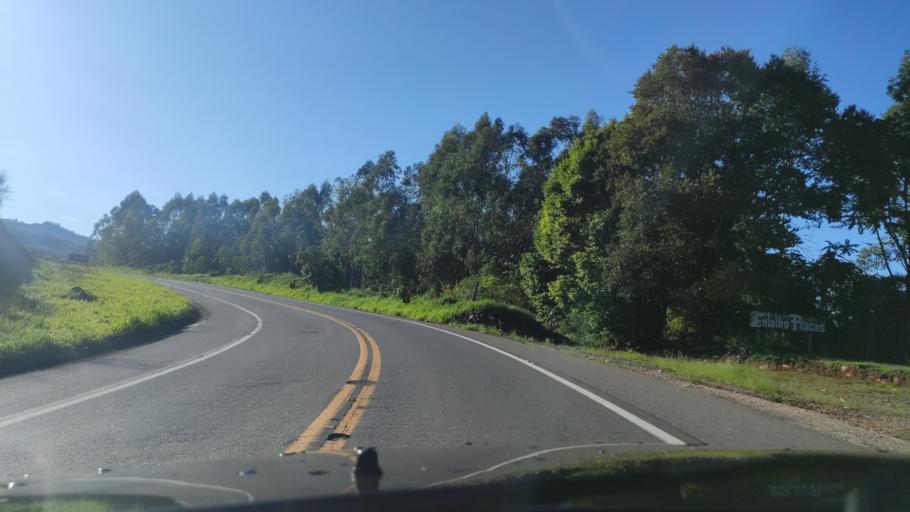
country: BR
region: Sao Paulo
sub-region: Aguas De Lindoia
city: Aguas de Lindoia
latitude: -22.5539
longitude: -46.6110
